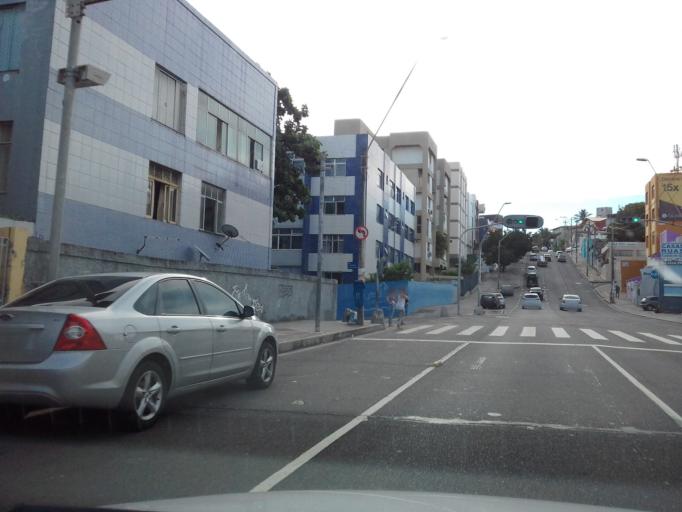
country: BR
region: Bahia
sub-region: Salvador
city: Salvador
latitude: -13.0119
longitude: -38.4710
